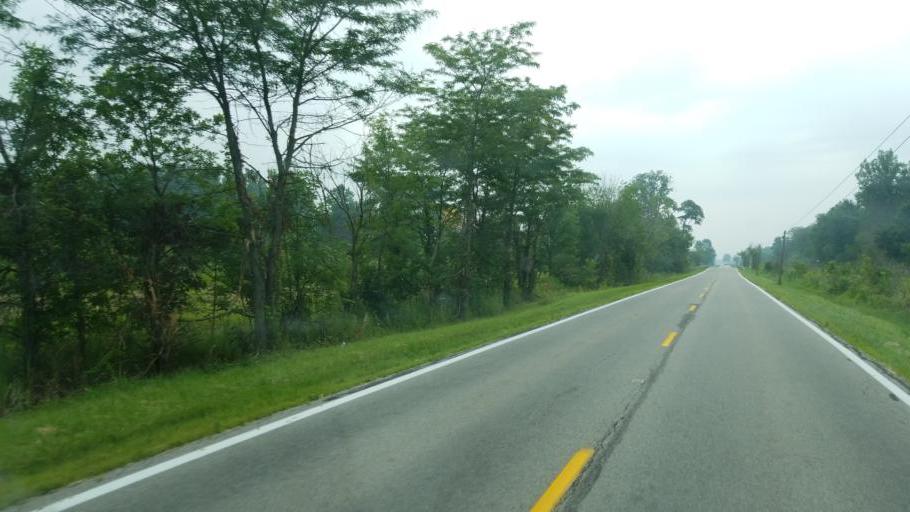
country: US
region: Ohio
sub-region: Marion County
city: Marion
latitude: 40.5860
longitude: -83.1960
